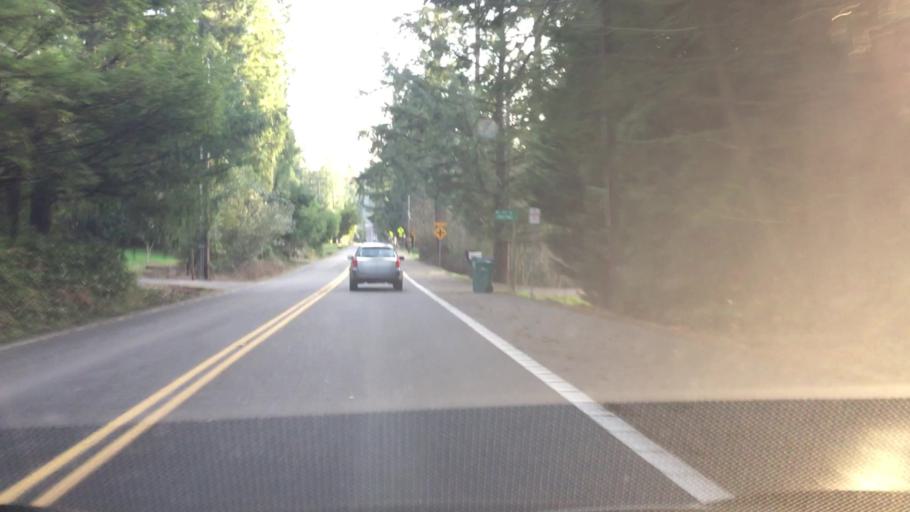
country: US
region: Washington
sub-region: King County
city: Woodinville
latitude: 47.7709
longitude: -122.1318
